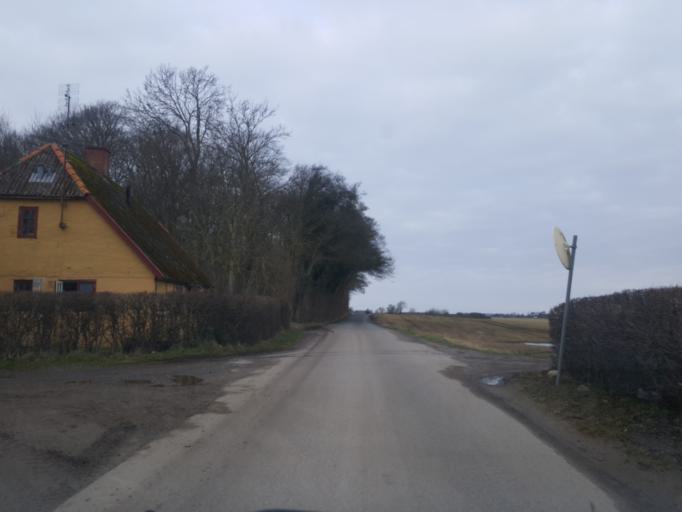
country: DK
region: Zealand
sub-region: Vordingborg Kommune
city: Neder Vindinge
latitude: 55.0336
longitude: 11.8456
